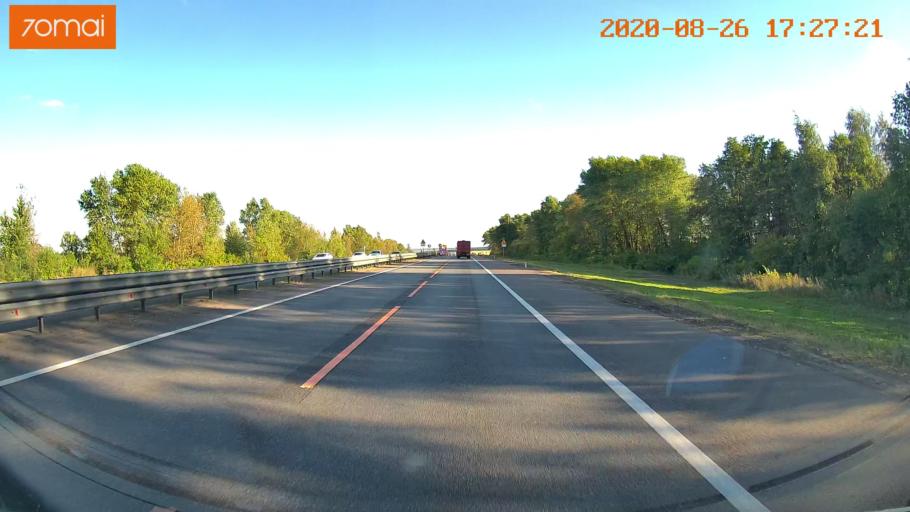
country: RU
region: Tula
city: Kazachka
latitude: 53.4739
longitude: 38.1241
